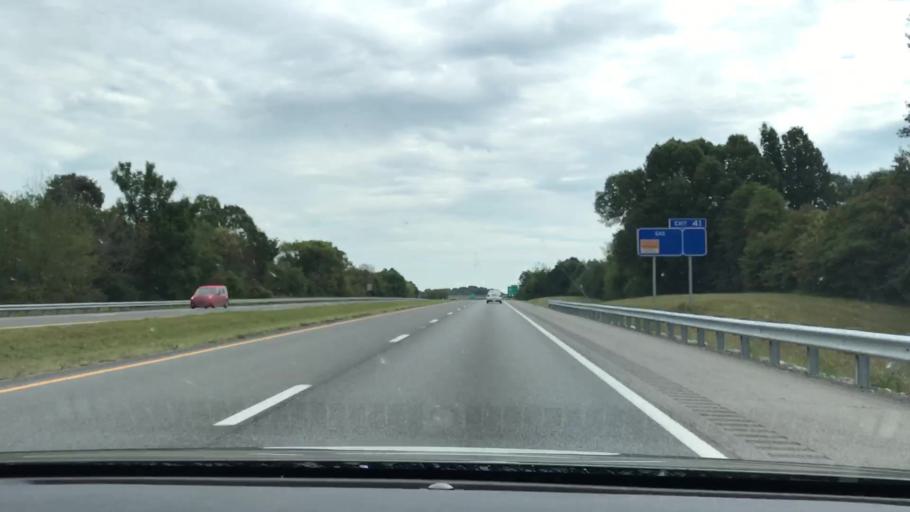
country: US
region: Kentucky
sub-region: Marshall County
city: Benton
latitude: 36.8475
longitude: -88.3888
